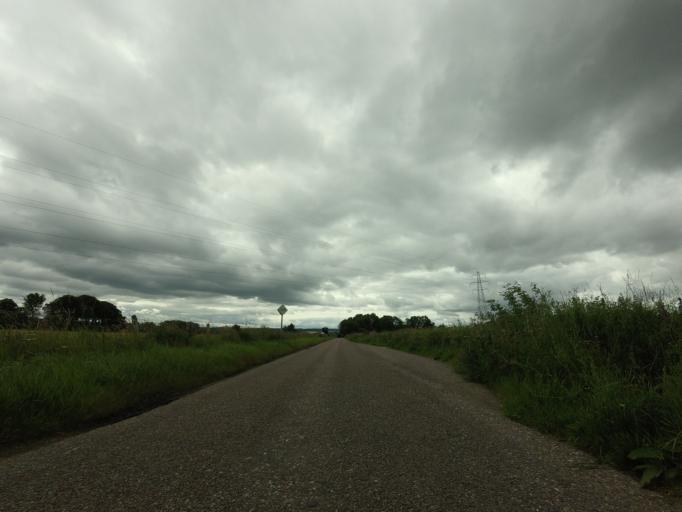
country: GB
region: Scotland
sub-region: Moray
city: Forres
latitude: 57.6124
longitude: -3.6853
